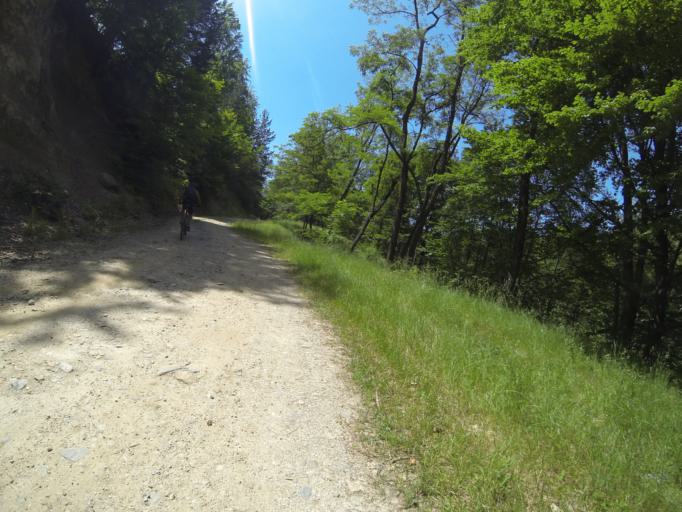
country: RO
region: Valcea
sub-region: Oras Baile Olanesti
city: Baile Olanesti
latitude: 45.2097
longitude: 24.2165
